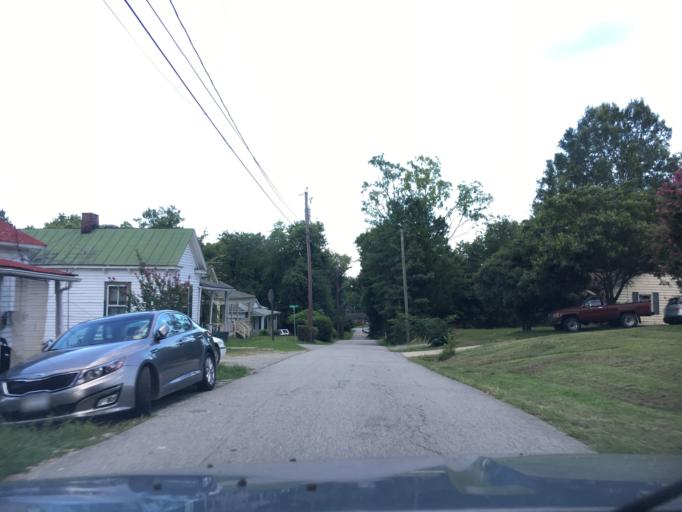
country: US
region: Virginia
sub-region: Halifax County
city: South Boston
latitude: 36.7122
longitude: -78.8992
